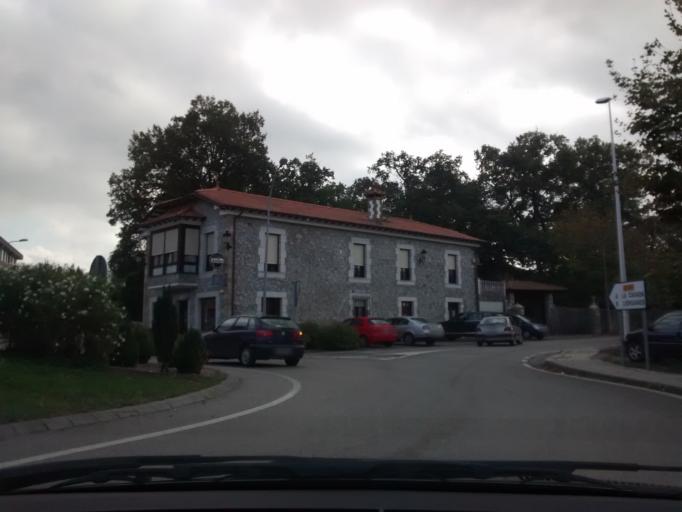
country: ES
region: Cantabria
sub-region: Provincia de Cantabria
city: Entrambasaguas
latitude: 43.3776
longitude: -3.6818
